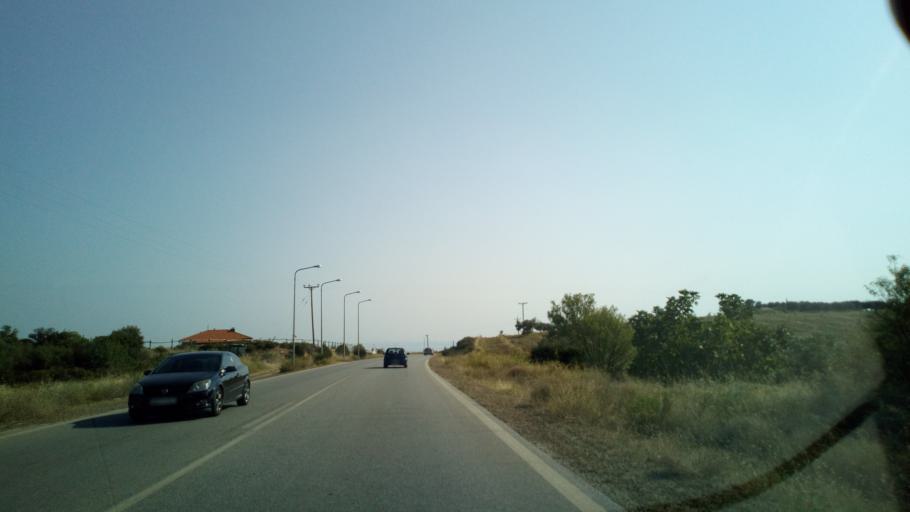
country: GR
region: Central Macedonia
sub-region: Nomos Chalkidikis
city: Polygyros
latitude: 40.3270
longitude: 23.4503
